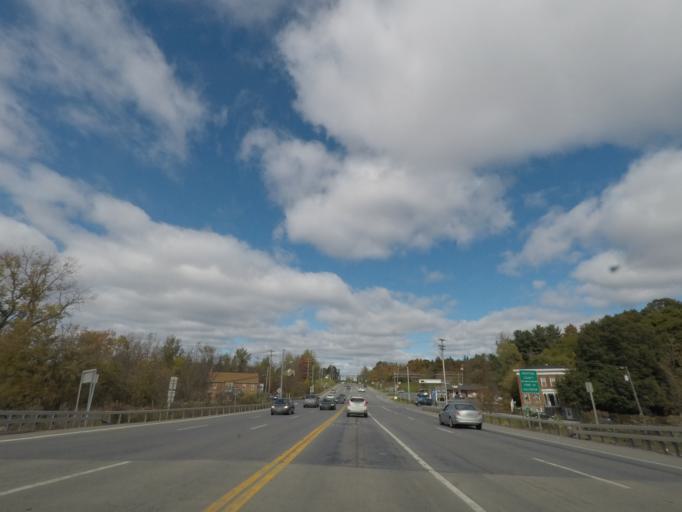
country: US
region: New York
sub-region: Albany County
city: Cohoes
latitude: 42.8229
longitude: -73.7324
